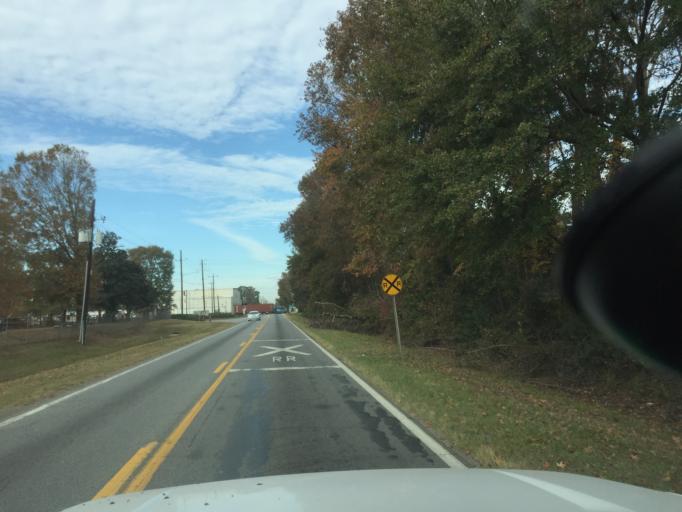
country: US
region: Georgia
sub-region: Chatham County
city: Savannah
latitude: 32.0845
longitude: -81.1325
